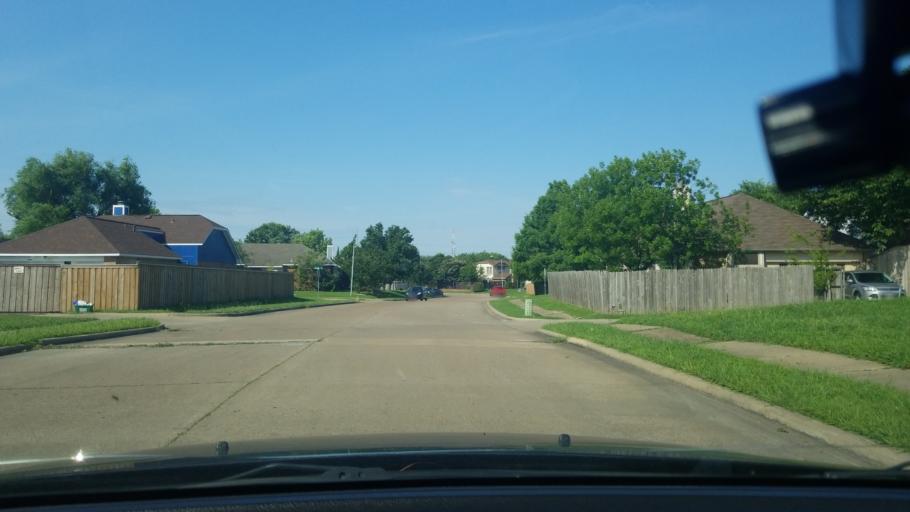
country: US
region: Texas
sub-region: Dallas County
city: Sunnyvale
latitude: 32.7777
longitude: -96.5752
